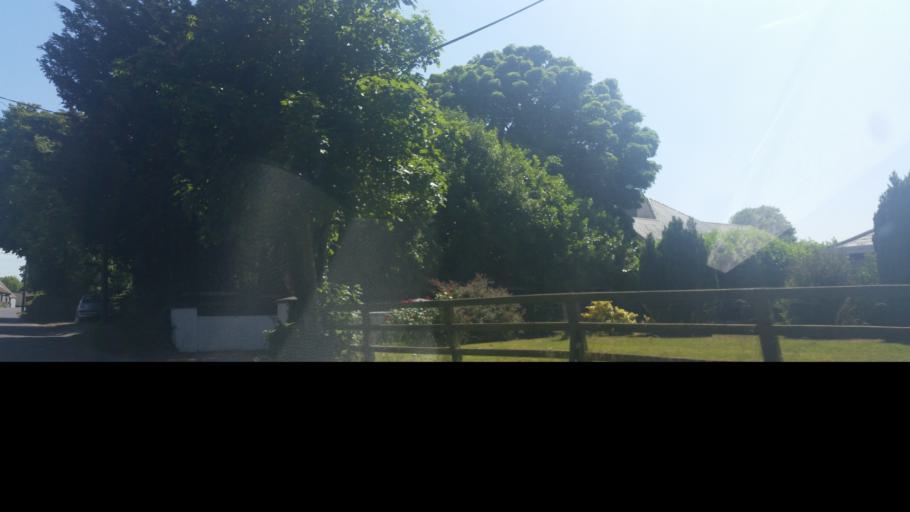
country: IE
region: Leinster
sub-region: An Mhi
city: Stamullin
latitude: 53.5773
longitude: -6.2842
